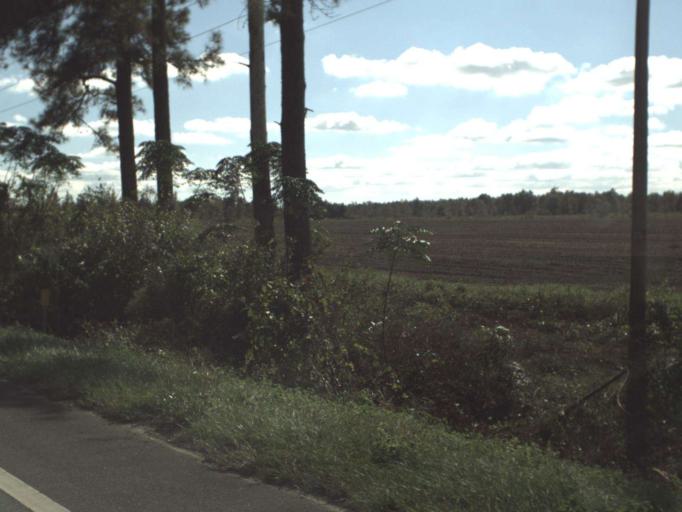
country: US
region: Florida
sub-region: Gulf County
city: Wewahitchka
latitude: 30.2069
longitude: -85.2089
